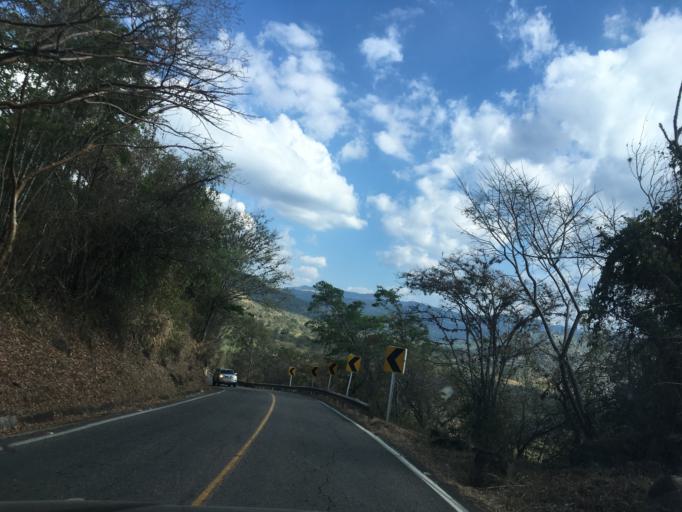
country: CO
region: Santander
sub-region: San Gil
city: San Gil
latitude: 6.5715
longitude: -73.1402
